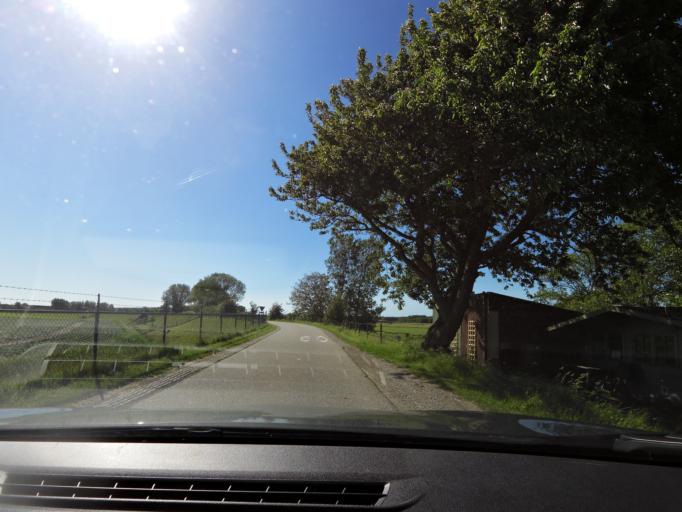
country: NL
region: South Holland
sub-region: Gemeente Hellevoetsluis
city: Nieuw-Helvoet
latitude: 51.8552
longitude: 4.1193
